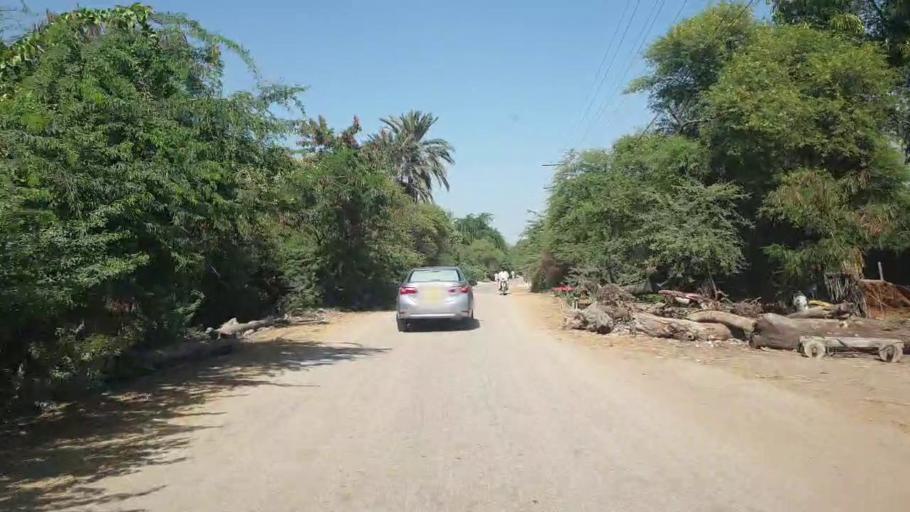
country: PK
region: Sindh
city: Talhar
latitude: 24.8854
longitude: 68.8201
